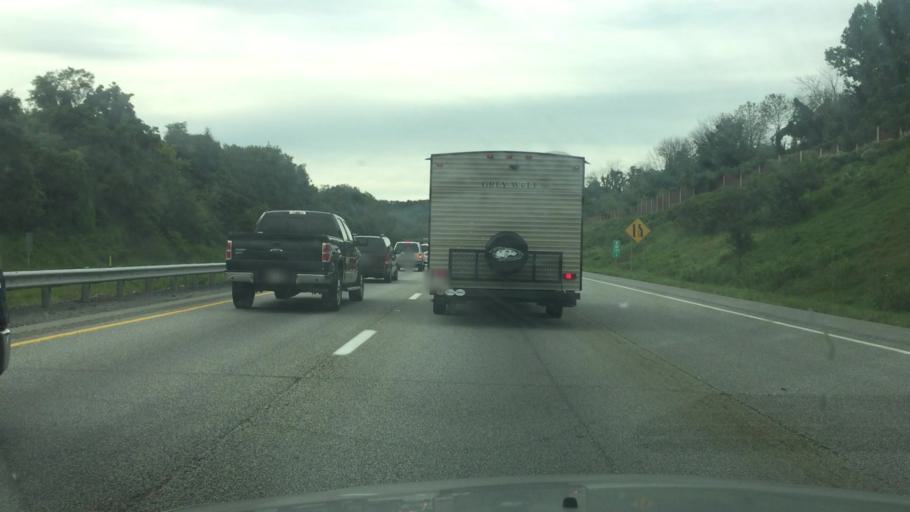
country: US
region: Pennsylvania
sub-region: Dauphin County
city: Harrisburg
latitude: 40.3148
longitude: -76.8819
